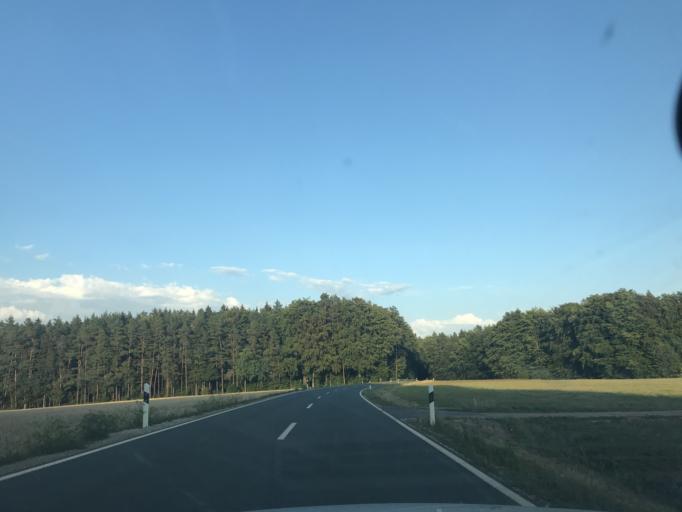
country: DE
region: Bavaria
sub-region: Upper Franconia
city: Pottenstein
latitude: 49.7123
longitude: 11.4202
